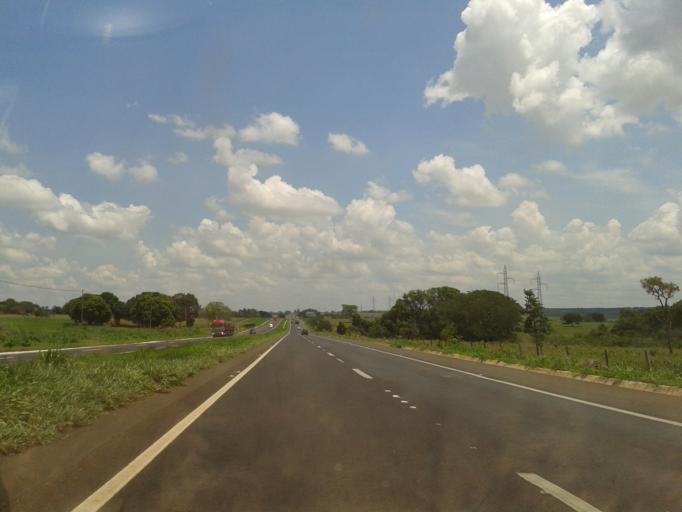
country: BR
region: Minas Gerais
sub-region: Uberlandia
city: Uberlandia
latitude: -18.8716
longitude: -48.5464
